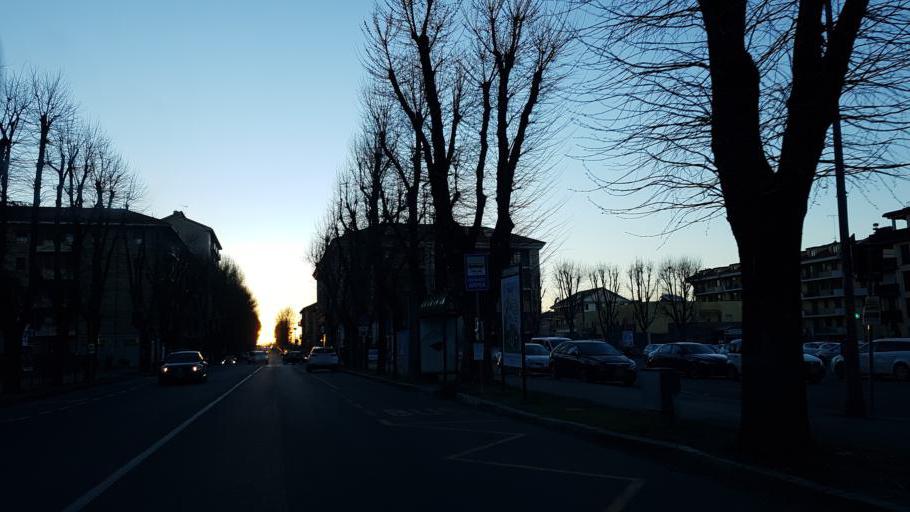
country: IT
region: Piedmont
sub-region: Provincia di Alessandria
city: Tortona
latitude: 44.8964
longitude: 8.8614
